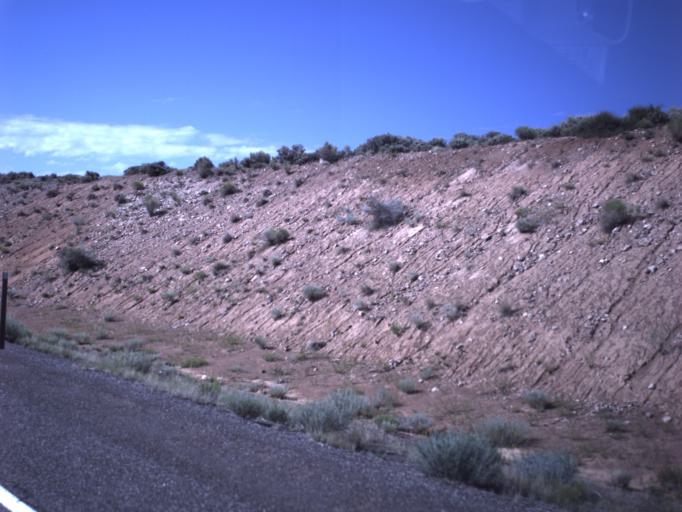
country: US
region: Utah
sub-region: Wayne County
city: Loa
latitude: 38.4607
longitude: -111.8352
